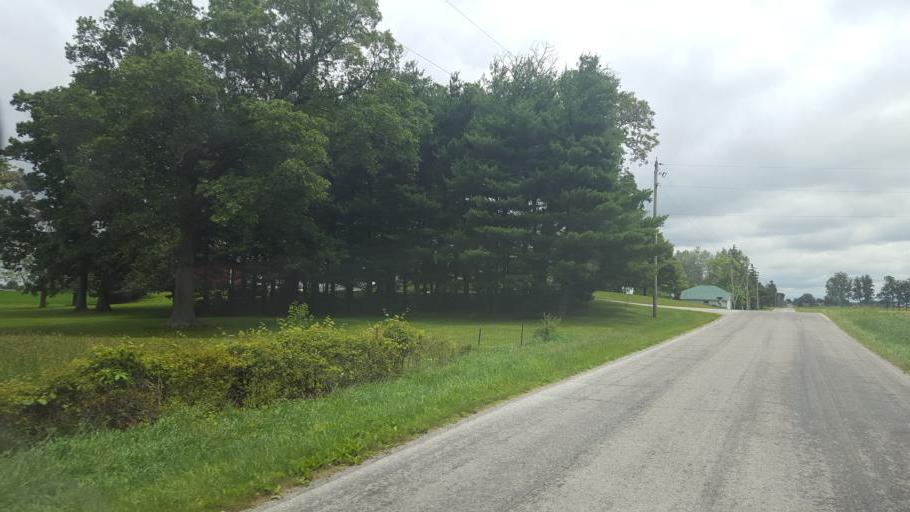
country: US
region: Ohio
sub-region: Crawford County
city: Bucyrus
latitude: 40.7756
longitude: -83.0196
